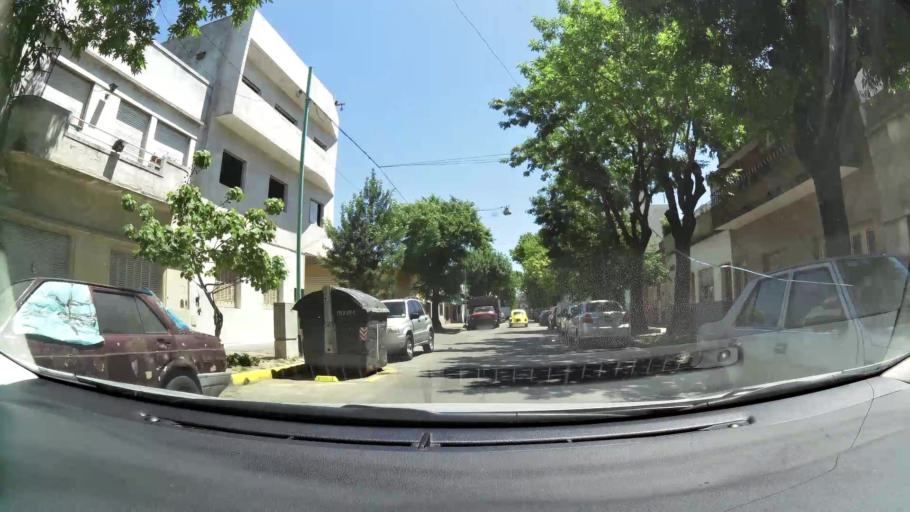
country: AR
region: Buenos Aires
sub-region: Partido de Avellaneda
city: Avellaneda
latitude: -34.6527
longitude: -58.3934
